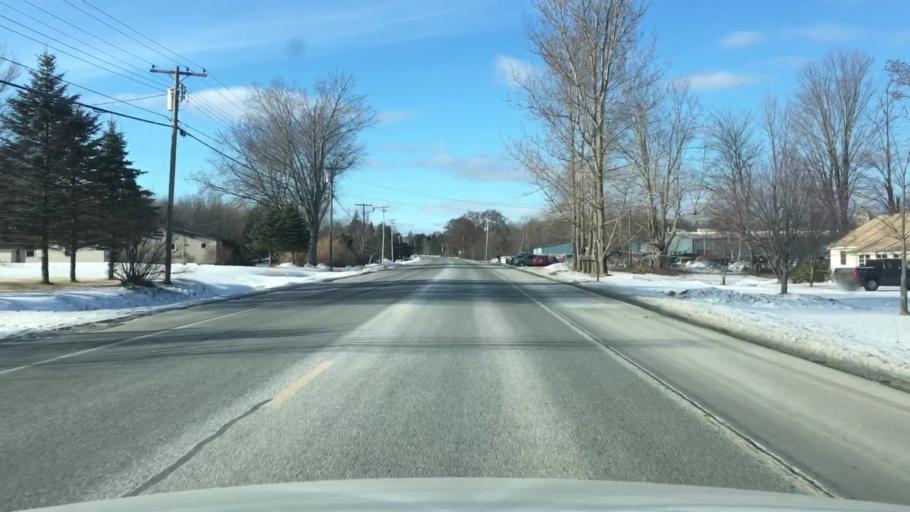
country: US
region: Maine
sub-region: Penobscot County
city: Eddington
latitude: 44.8239
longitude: -68.6524
